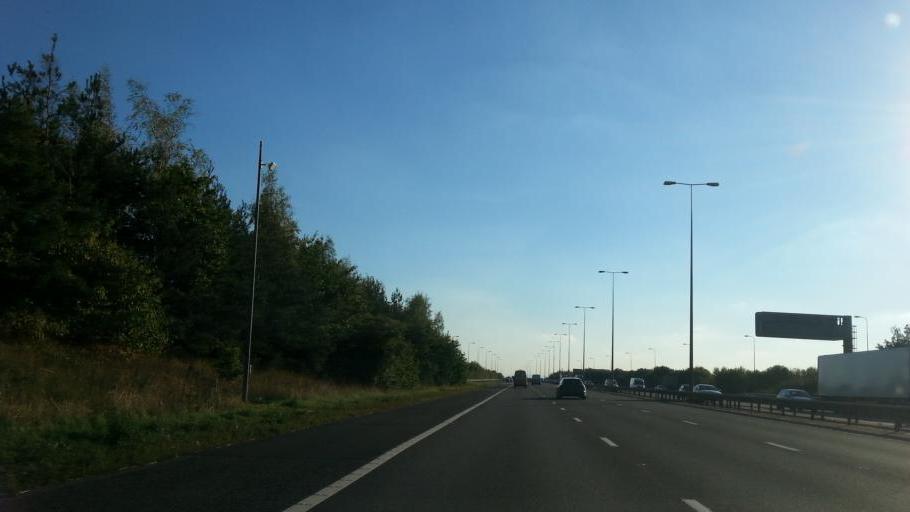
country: GB
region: England
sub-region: Worcestershire
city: Worcester
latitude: 52.1668
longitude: -2.1818
